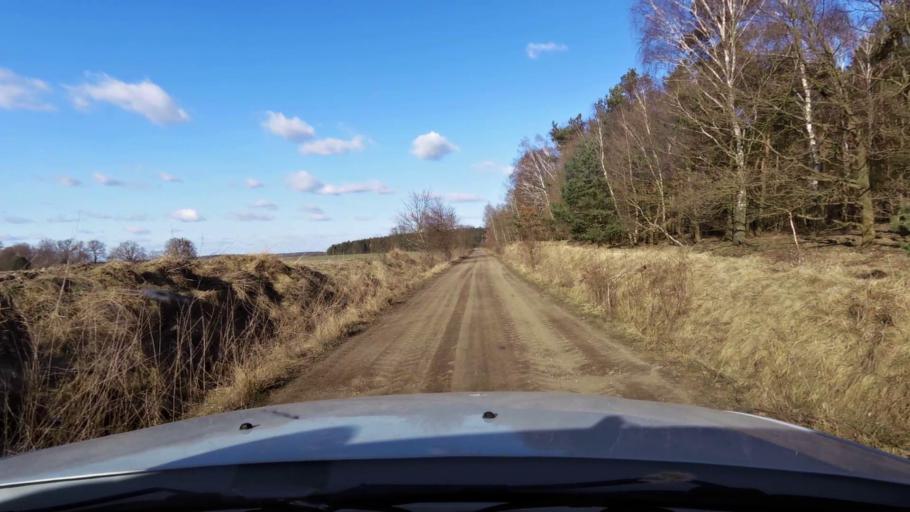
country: PL
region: West Pomeranian Voivodeship
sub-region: Powiat choszczenski
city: Choszczno
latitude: 53.1587
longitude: 15.3769
